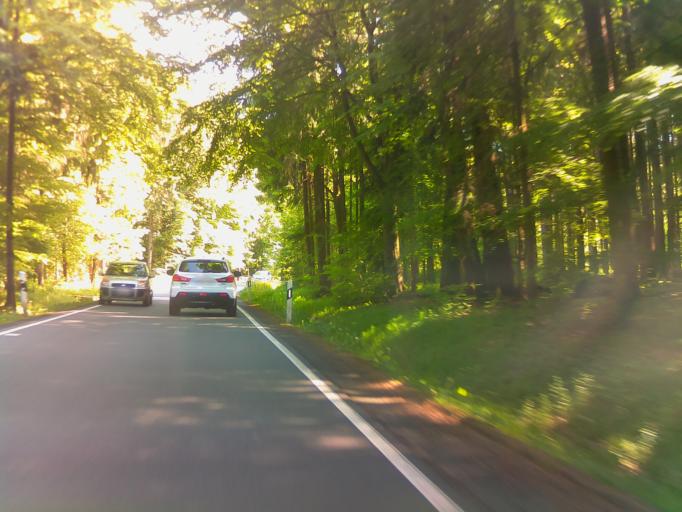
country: DE
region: Hesse
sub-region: Regierungsbezirk Darmstadt
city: Lutzelbach
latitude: 49.7095
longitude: 9.0859
